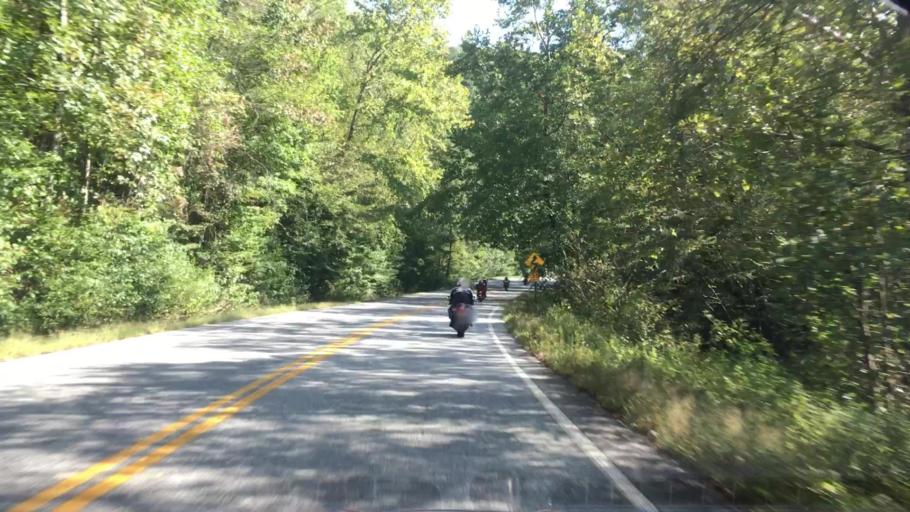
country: US
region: Georgia
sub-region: White County
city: Cleveland
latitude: 34.6720
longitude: -83.9023
